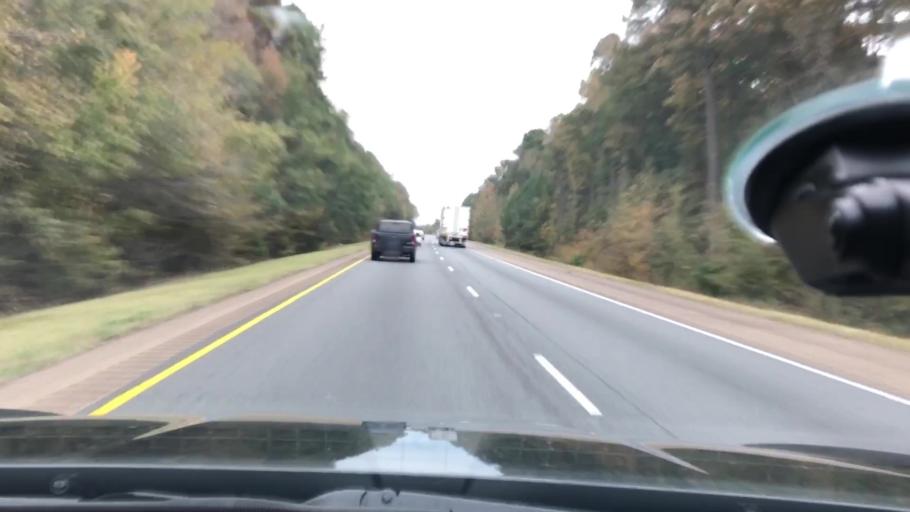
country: US
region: Arkansas
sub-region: Clark County
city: Gurdon
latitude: 33.9187
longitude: -93.2760
